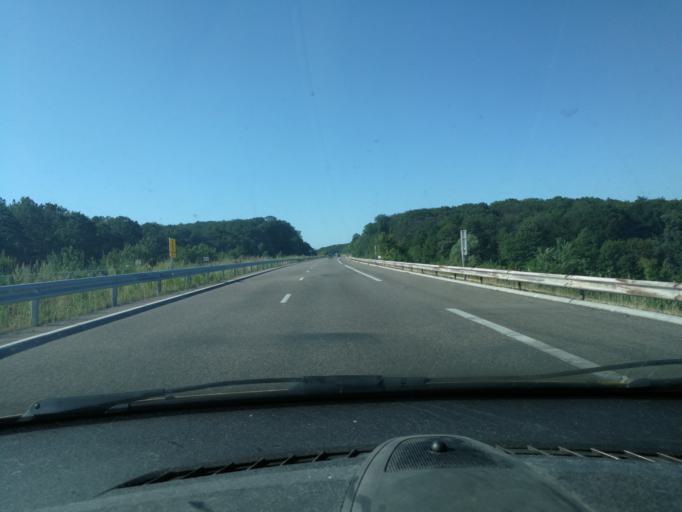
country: FR
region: Alsace
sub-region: Departement du Bas-Rhin
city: Sarrewerden
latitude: 48.8904
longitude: 7.1239
